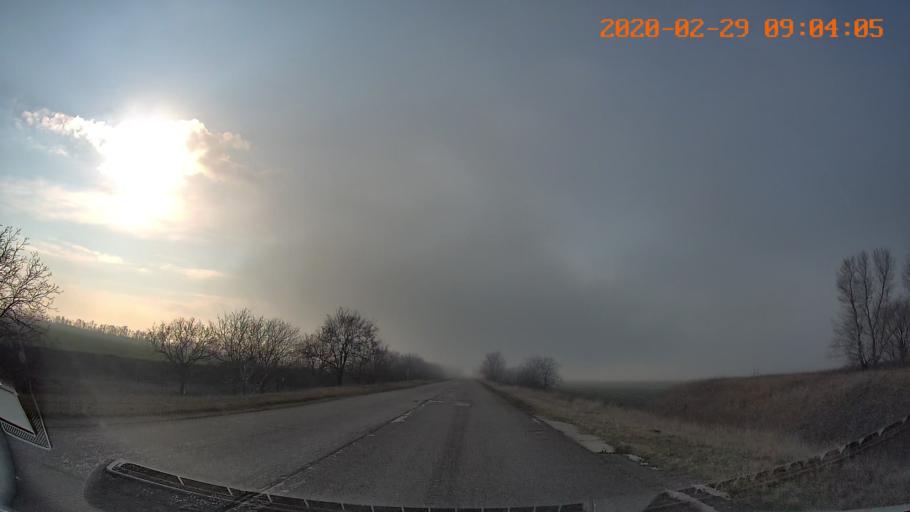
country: UA
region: Odessa
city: Velykoploske
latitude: 46.9074
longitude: 29.7345
